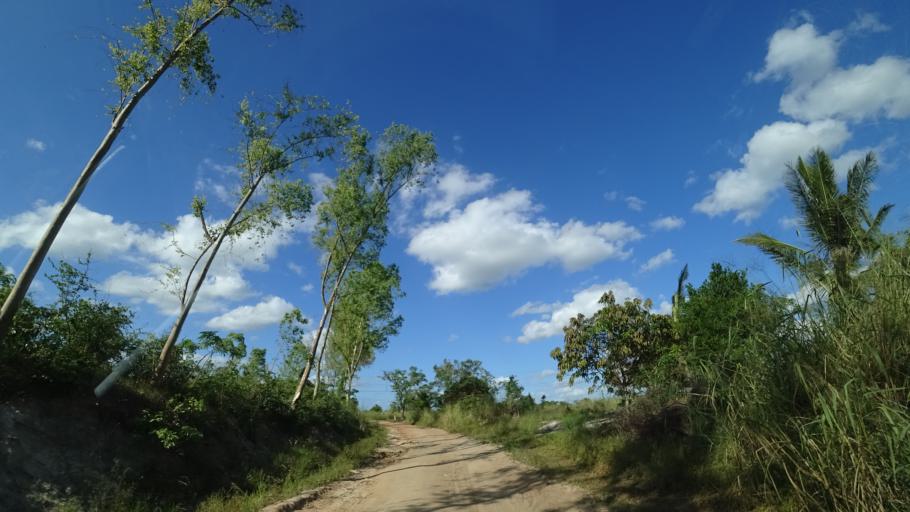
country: MZ
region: Sofala
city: Dondo
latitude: -19.4237
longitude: 34.7106
